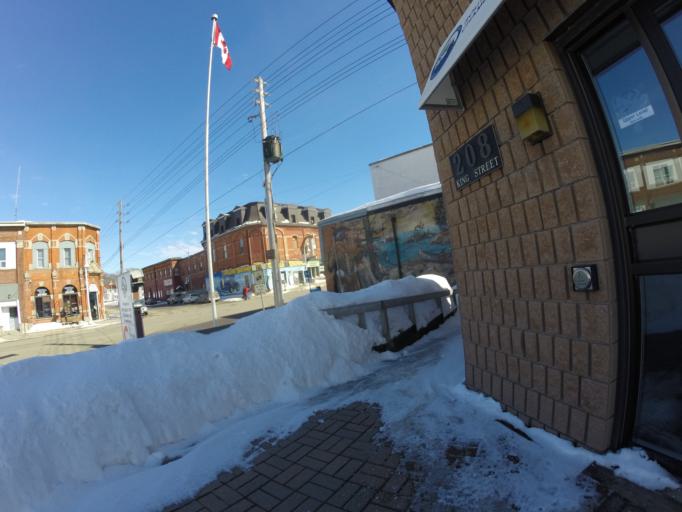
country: CA
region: Ontario
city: Midland
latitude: 44.7517
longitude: -79.8874
